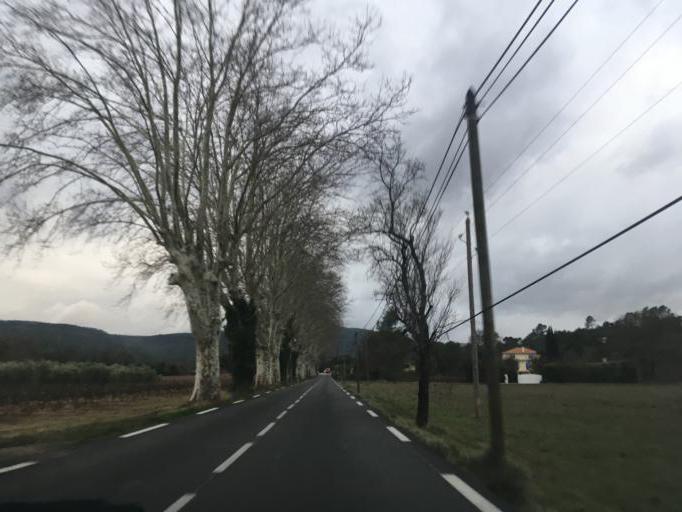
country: FR
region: Provence-Alpes-Cote d'Azur
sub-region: Departement du Var
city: Besse-sur-Issole
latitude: 43.3425
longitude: 6.1689
